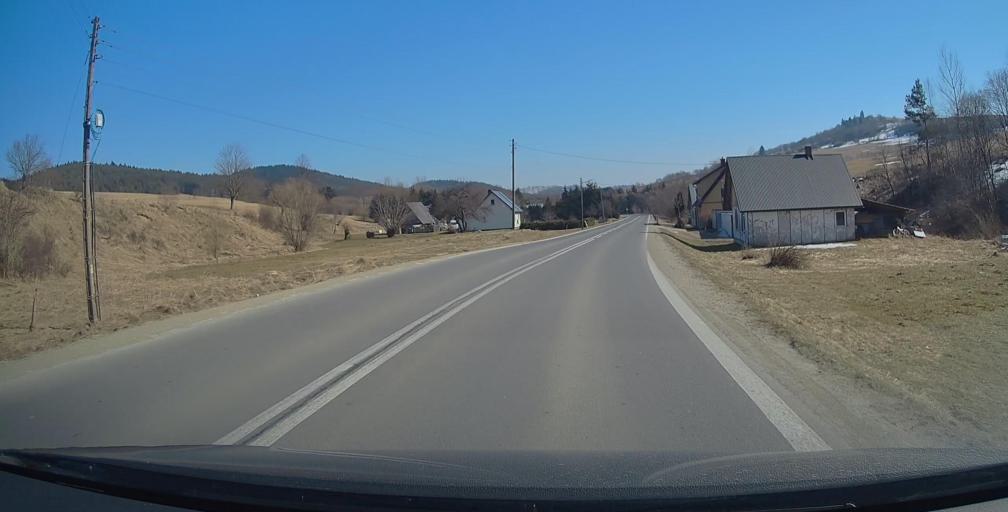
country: PL
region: Subcarpathian Voivodeship
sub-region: Powiat bieszczadzki
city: Ustrzyki Dolne
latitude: 49.4941
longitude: 22.6383
